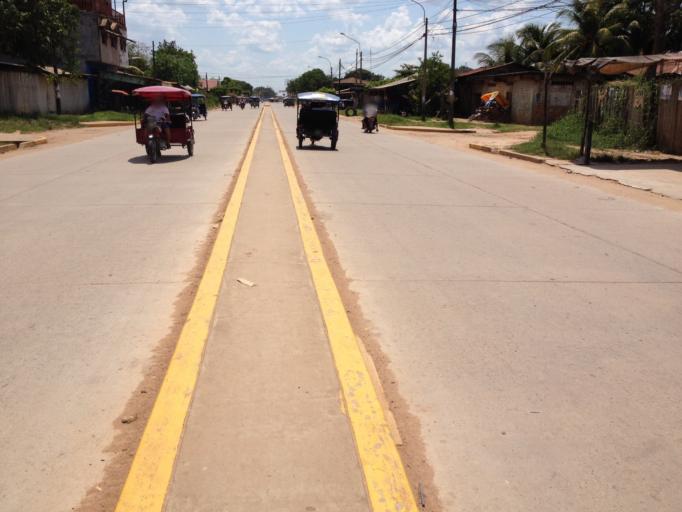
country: PE
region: Ucayali
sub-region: Provincia de Coronel Portillo
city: Pucallpa
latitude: -8.3804
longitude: -74.5573
